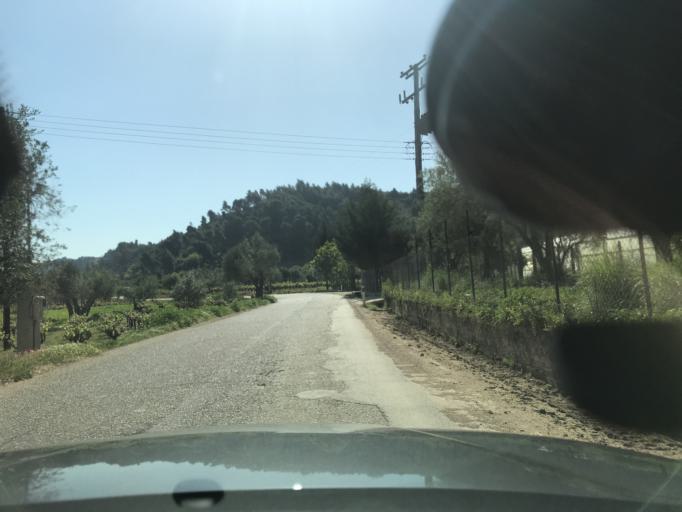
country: GR
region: West Greece
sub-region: Nomos Ileias
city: Alfiousa
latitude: 37.6412
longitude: 21.5223
